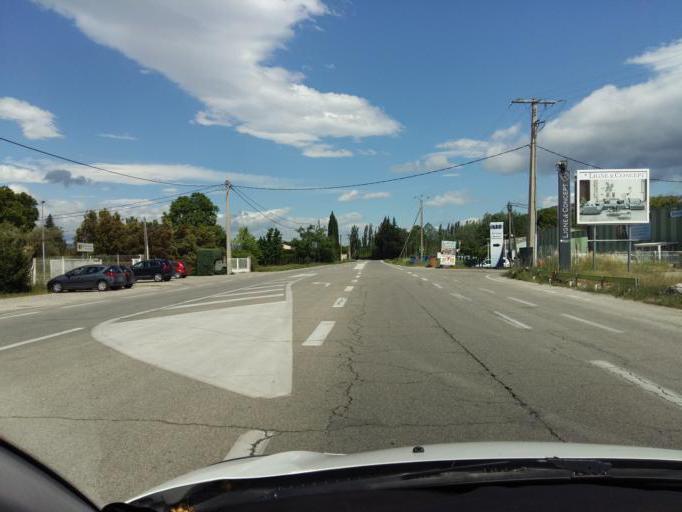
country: FR
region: Provence-Alpes-Cote d'Azur
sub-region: Departement du Vaucluse
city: Taillades
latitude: 43.8415
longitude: 5.0665
